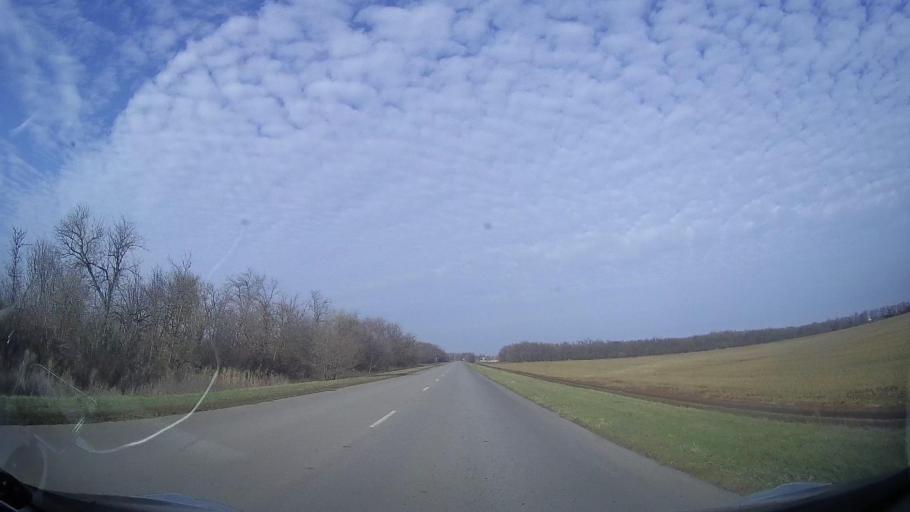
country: RU
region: Rostov
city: Gigant
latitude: 46.8297
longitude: 41.3367
